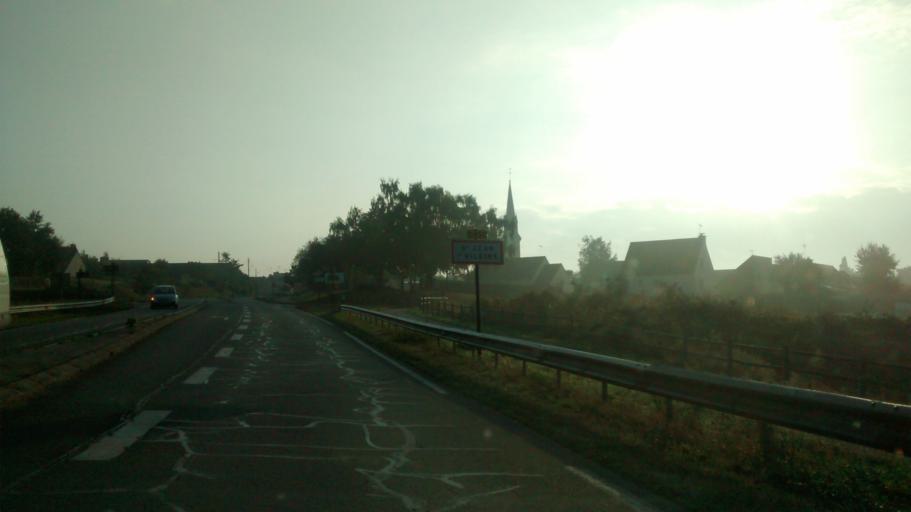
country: FR
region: Brittany
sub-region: Departement d'Ille-et-Vilaine
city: Saint-Didier
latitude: 48.1164
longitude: -1.3656
